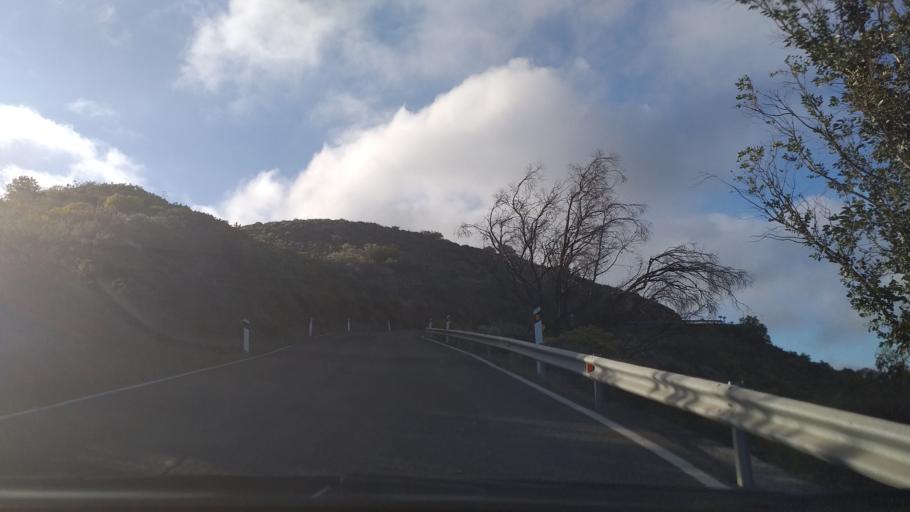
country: ES
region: Canary Islands
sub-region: Provincia de Las Palmas
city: Valsequillo de Gran Canaria
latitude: 27.9560
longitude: -15.4945
